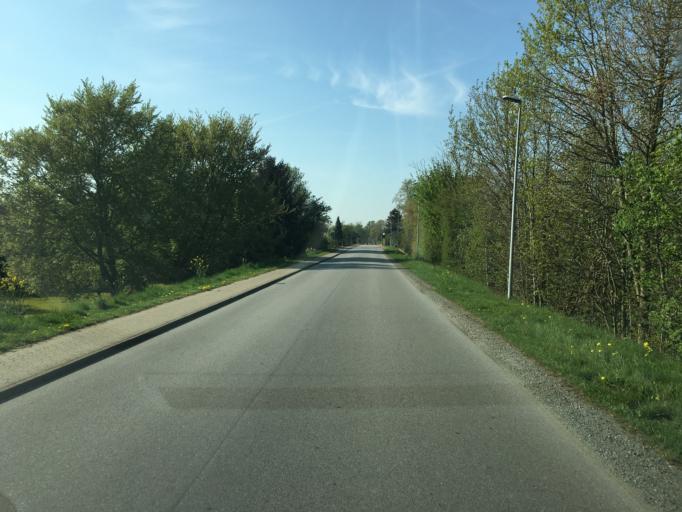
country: DK
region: South Denmark
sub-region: Haderslev Kommune
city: Vojens
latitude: 55.2450
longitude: 9.3166
